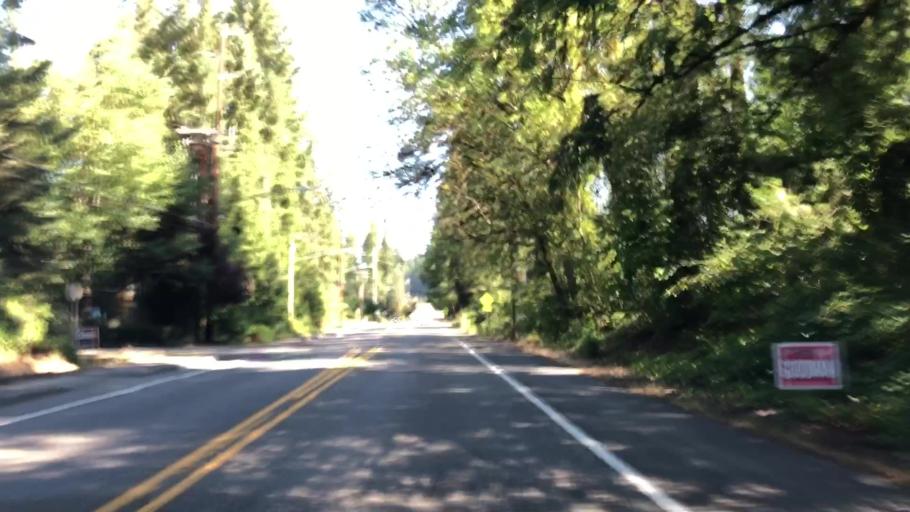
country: US
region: Washington
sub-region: King County
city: Cottage Lake
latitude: 47.7503
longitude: -122.0817
